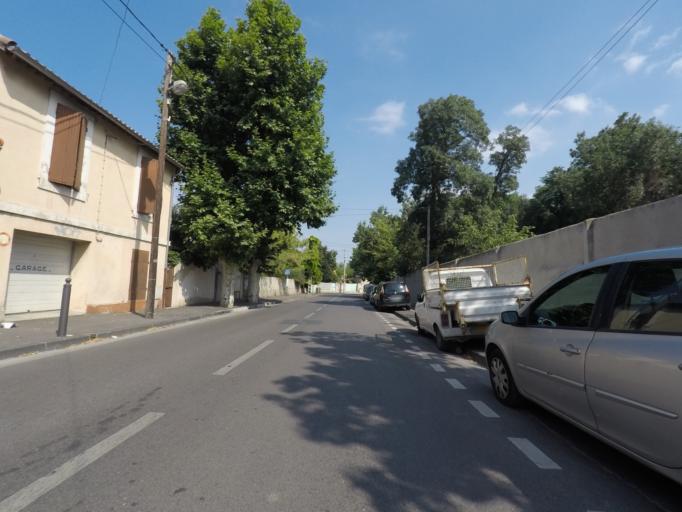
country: FR
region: Provence-Alpes-Cote d'Azur
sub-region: Departement des Bouches-du-Rhone
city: Marseille 10
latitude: 43.2718
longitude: 5.4068
